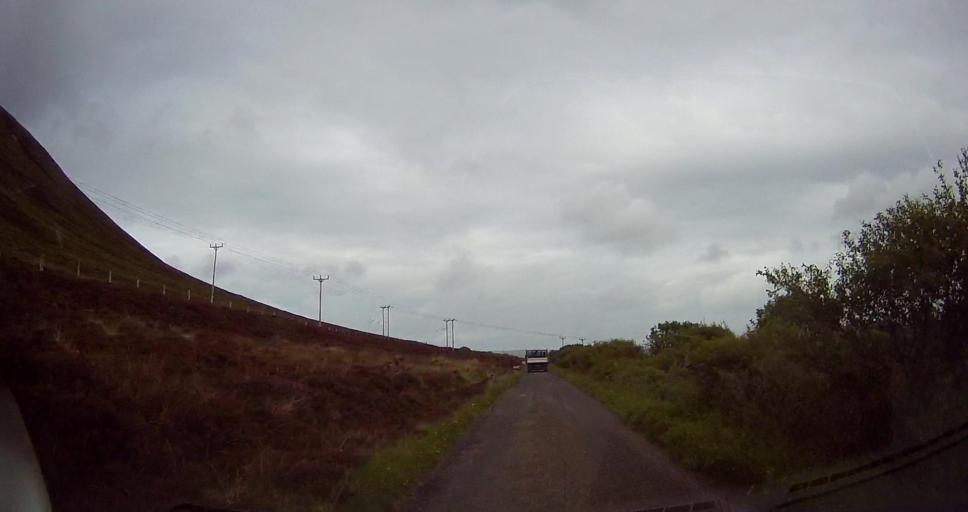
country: GB
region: Scotland
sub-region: Orkney Islands
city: Stromness
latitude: 58.8949
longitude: -3.3143
